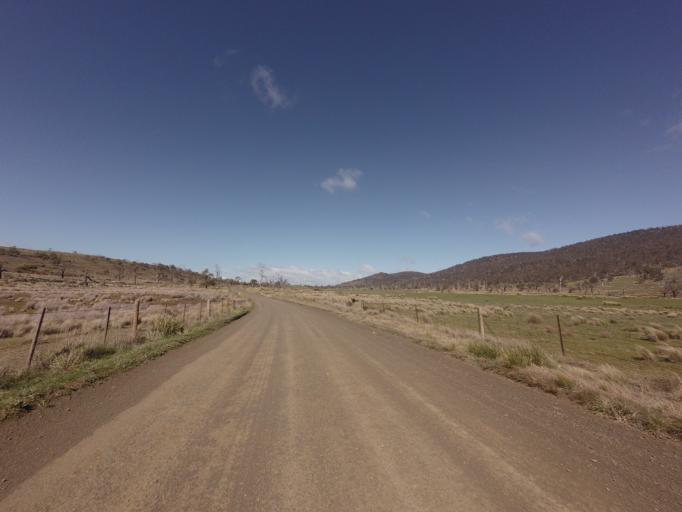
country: AU
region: Tasmania
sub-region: Northern Midlands
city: Evandale
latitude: -41.9310
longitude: 147.4156
